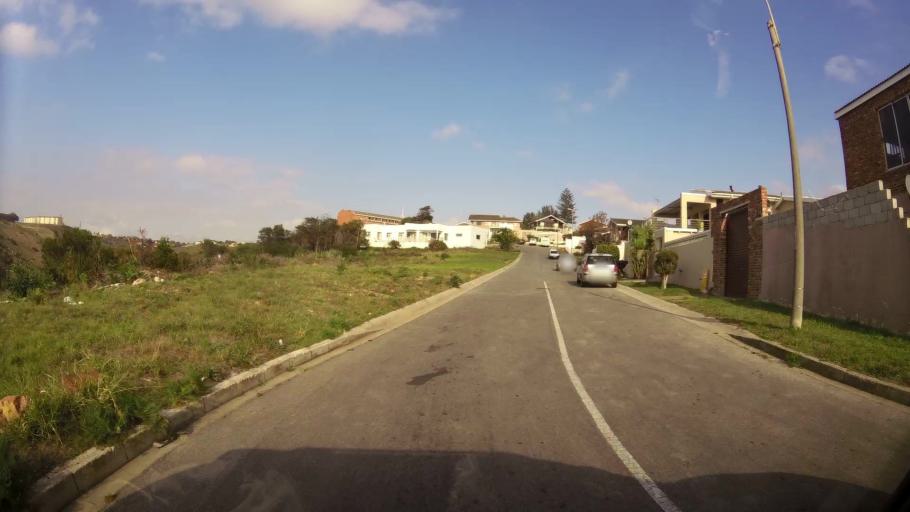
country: ZA
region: Eastern Cape
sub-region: Nelson Mandela Bay Metropolitan Municipality
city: Port Elizabeth
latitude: -33.9269
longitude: 25.5579
